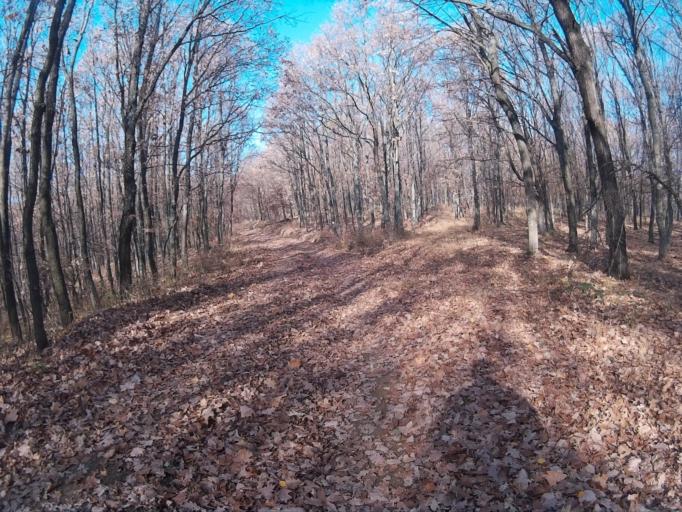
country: HU
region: Heves
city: Belapatfalva
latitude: 48.0236
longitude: 20.3961
